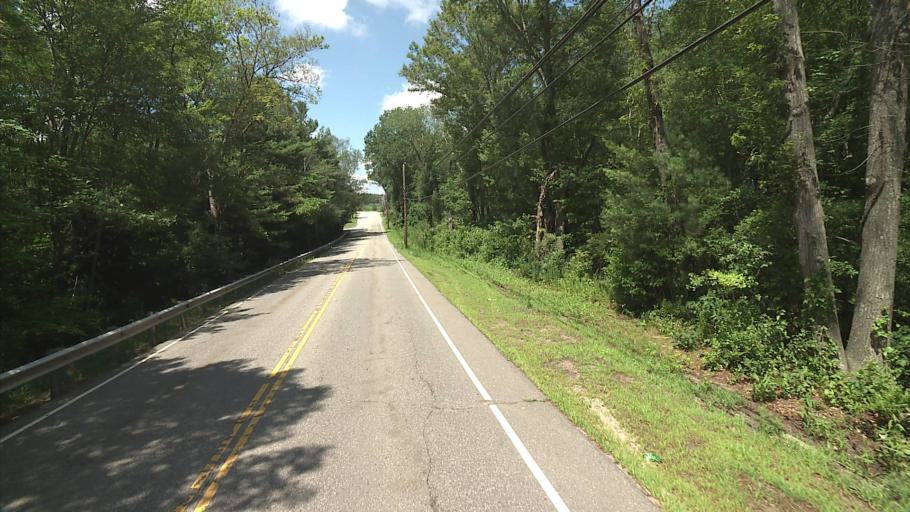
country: US
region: Connecticut
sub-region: Windham County
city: Windham
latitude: 41.7000
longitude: -72.1408
